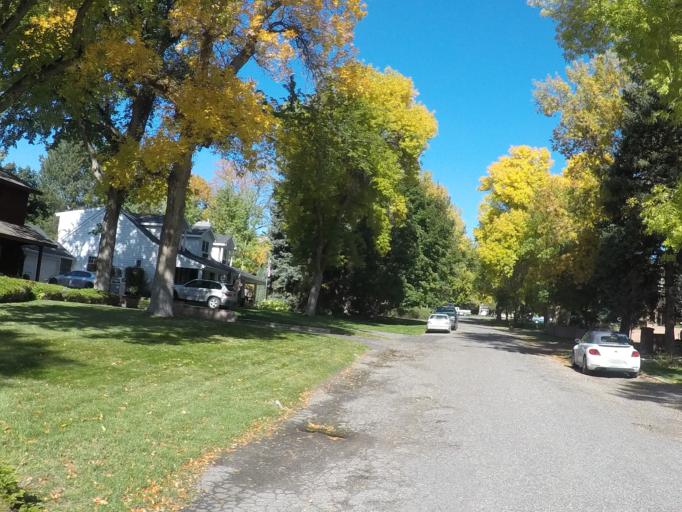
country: US
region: Montana
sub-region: Yellowstone County
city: Billings
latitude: 45.7957
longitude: -108.5309
